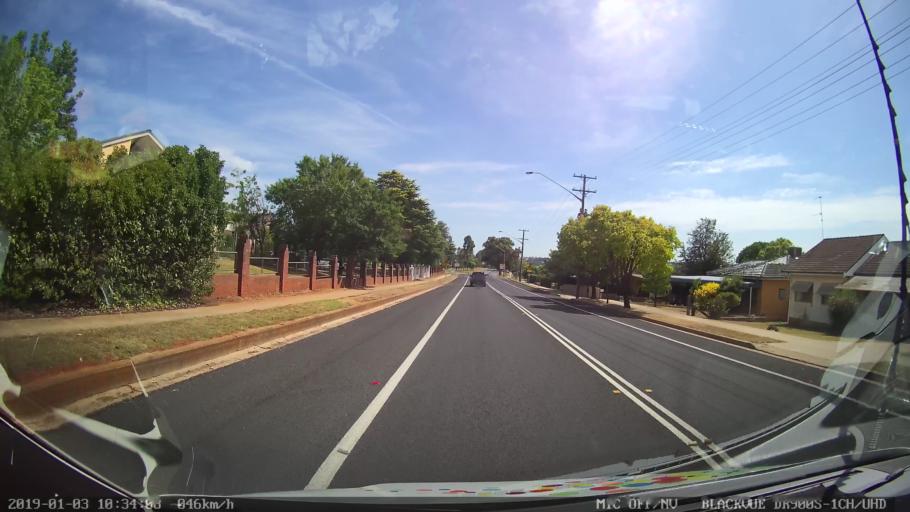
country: AU
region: New South Wales
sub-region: Young
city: Young
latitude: -34.3236
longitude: 148.2907
